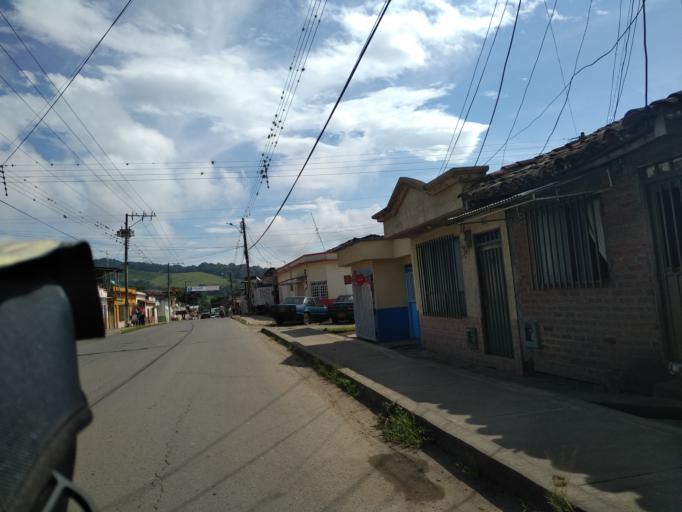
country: CO
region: Valle del Cauca
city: Caicedonia
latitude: 4.3369
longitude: -75.8288
